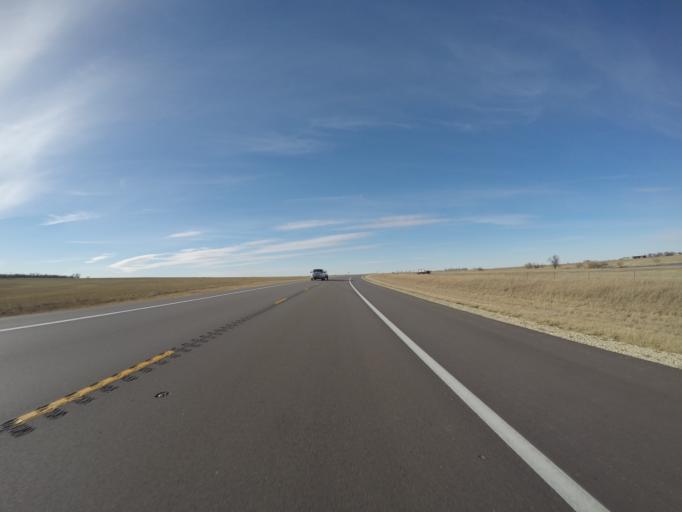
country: US
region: Kansas
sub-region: Marion County
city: Hillsboro
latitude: 38.3643
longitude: -97.3558
